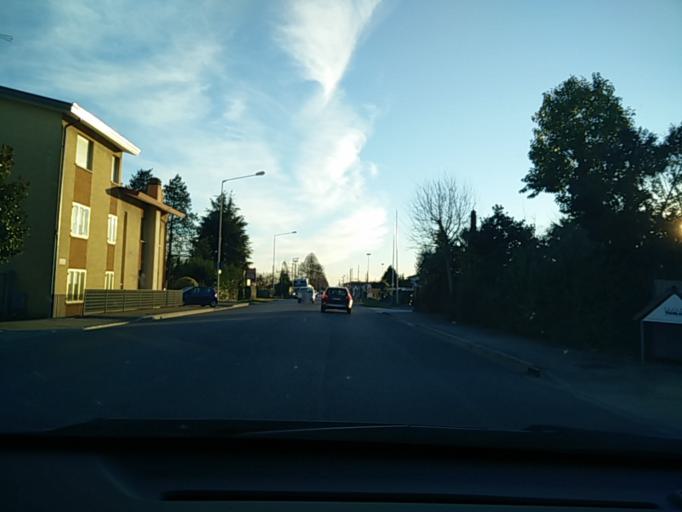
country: IT
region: Friuli Venezia Giulia
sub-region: Provincia di Udine
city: Pasian di Prato
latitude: 46.0425
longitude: 13.1919
